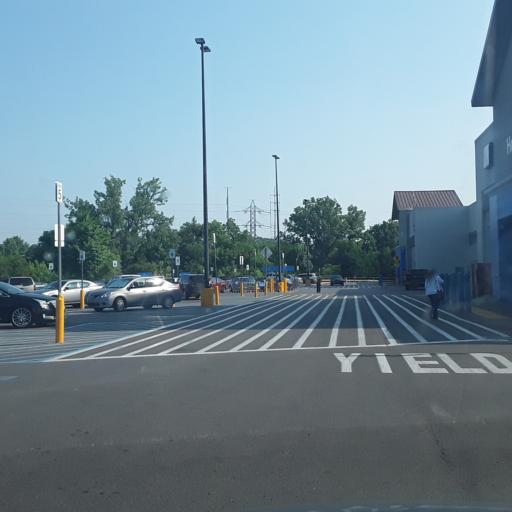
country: US
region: Tennessee
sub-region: Williamson County
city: Brentwood Estates
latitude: 36.0415
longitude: -86.7099
